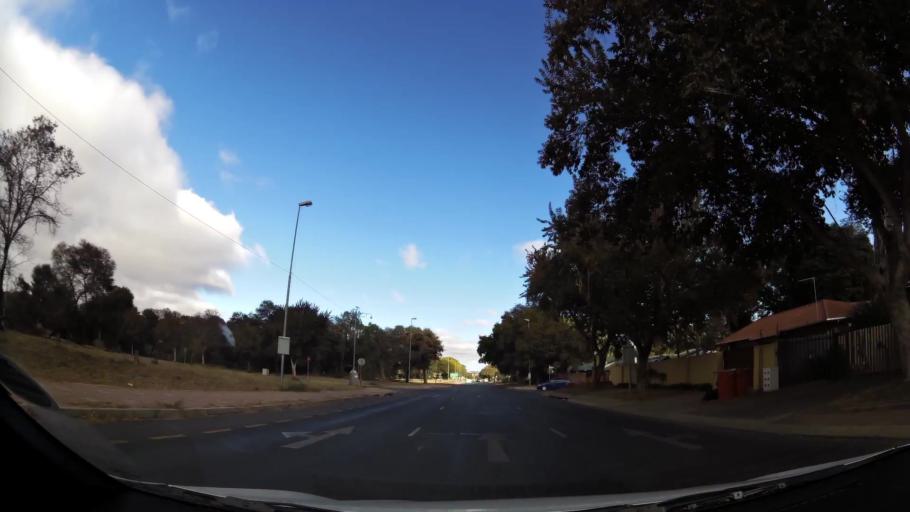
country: ZA
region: Limpopo
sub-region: Capricorn District Municipality
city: Polokwane
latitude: -23.9181
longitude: 29.4658
